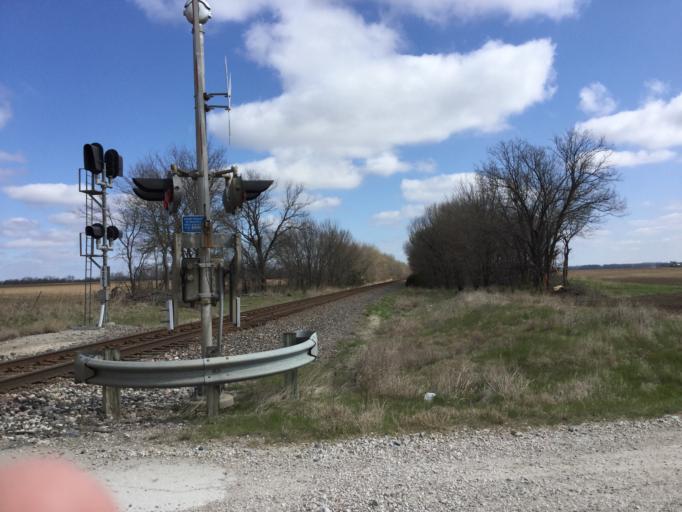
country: US
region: Kansas
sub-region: Wilson County
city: Neodesha
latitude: 37.3704
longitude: -95.6970
